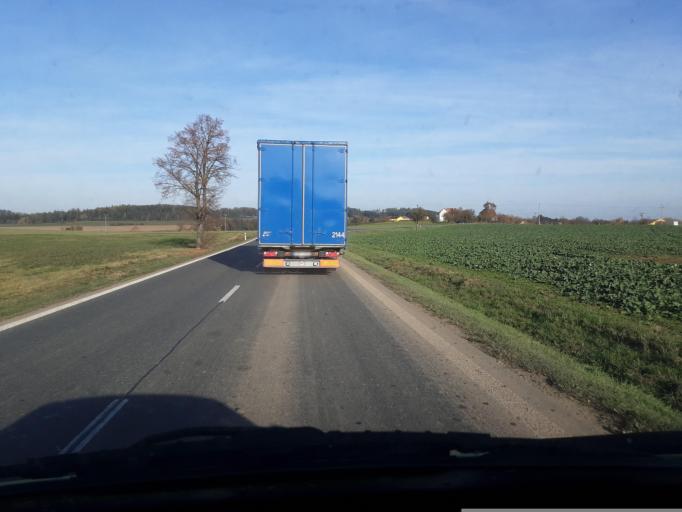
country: CZ
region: Plzensky
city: Horazd'ovice
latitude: 49.3273
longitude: 13.6386
